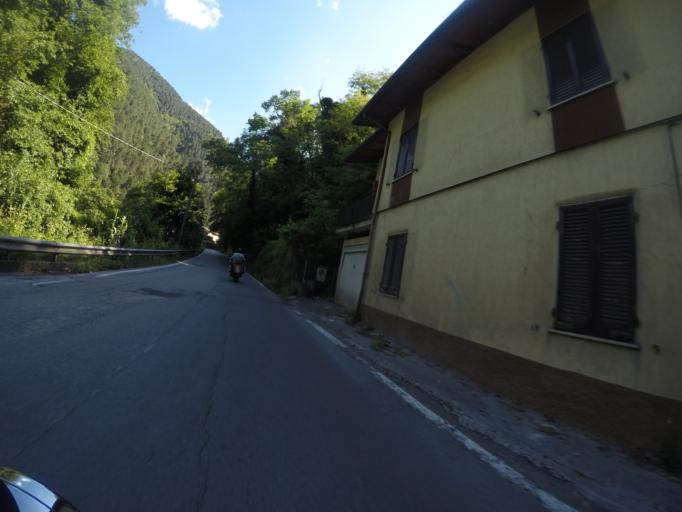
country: IT
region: Tuscany
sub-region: Provincia di Massa-Carrara
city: Montignoso
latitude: 44.0461
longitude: 10.1545
